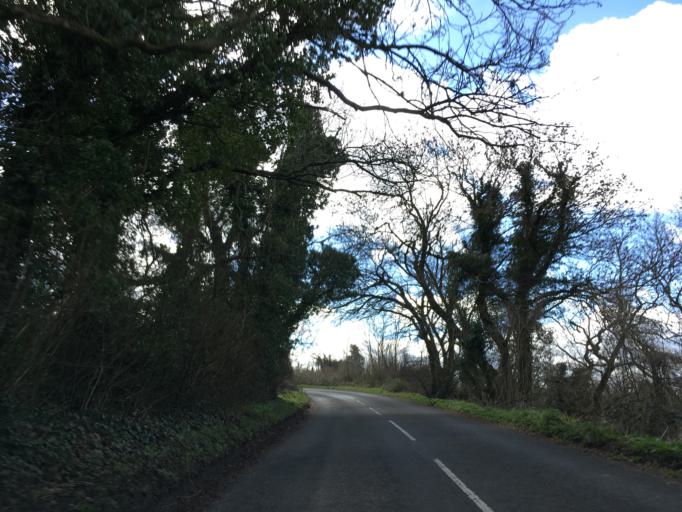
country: GB
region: England
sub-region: South Gloucestershire
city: Horton
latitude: 51.5939
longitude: -2.3345
